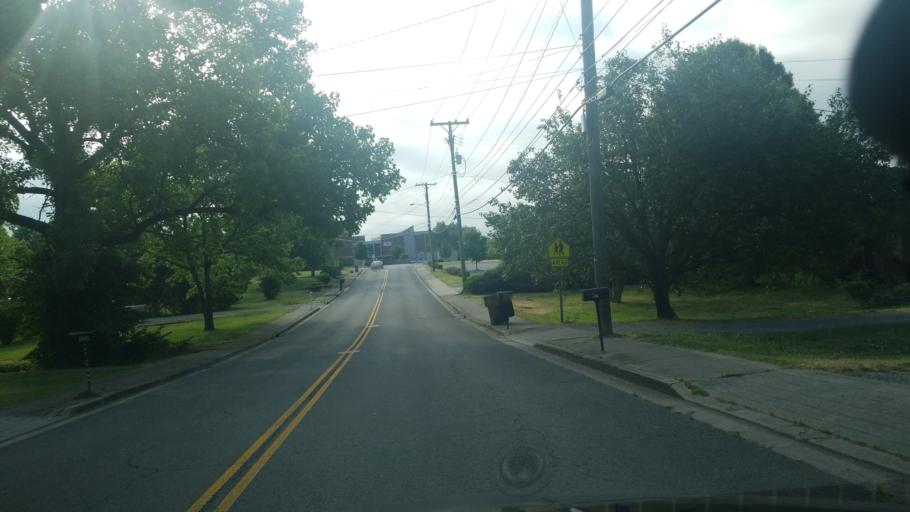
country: US
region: Tennessee
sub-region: Davidson County
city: Nashville
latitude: 36.2323
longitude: -86.7526
